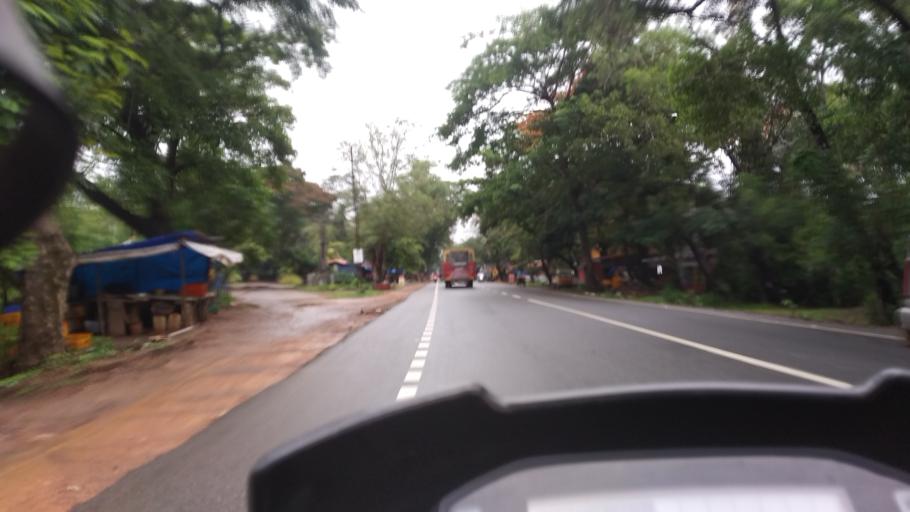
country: IN
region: Kerala
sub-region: Alappuzha
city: Mavelikara
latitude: 9.2881
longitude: 76.4384
